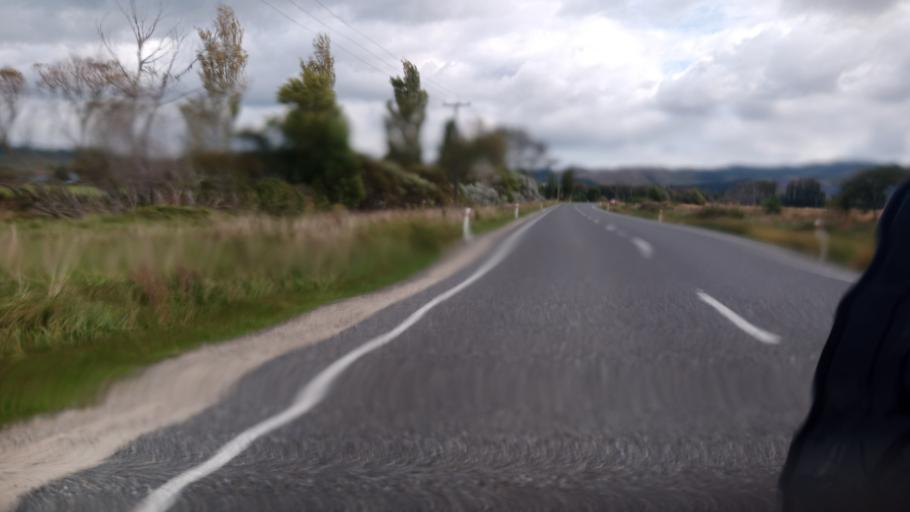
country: NZ
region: Gisborne
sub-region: Gisborne District
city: Gisborne
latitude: -38.3343
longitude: 178.2829
